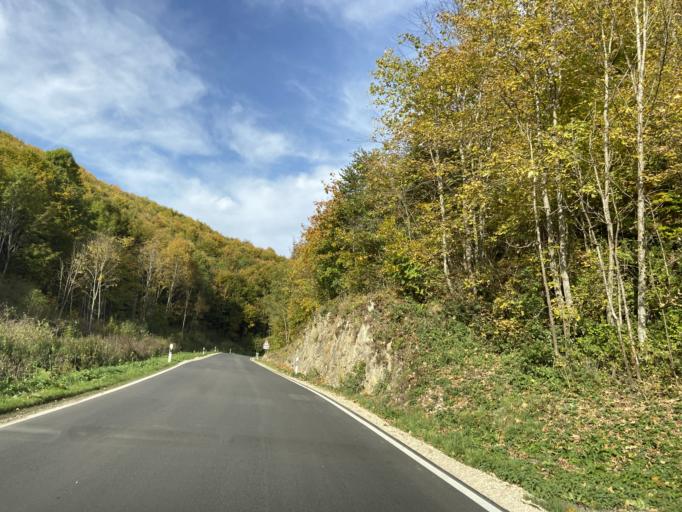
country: DE
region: Baden-Wuerttemberg
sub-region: Tuebingen Region
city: Leibertingen
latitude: 48.0644
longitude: 9.0362
